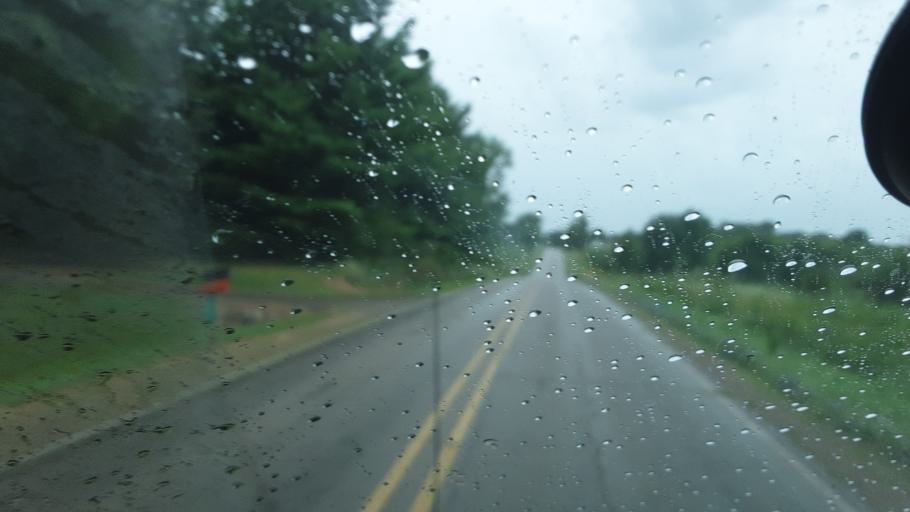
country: US
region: Ohio
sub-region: Williams County
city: Pioneer
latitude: 41.7090
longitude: -84.6077
